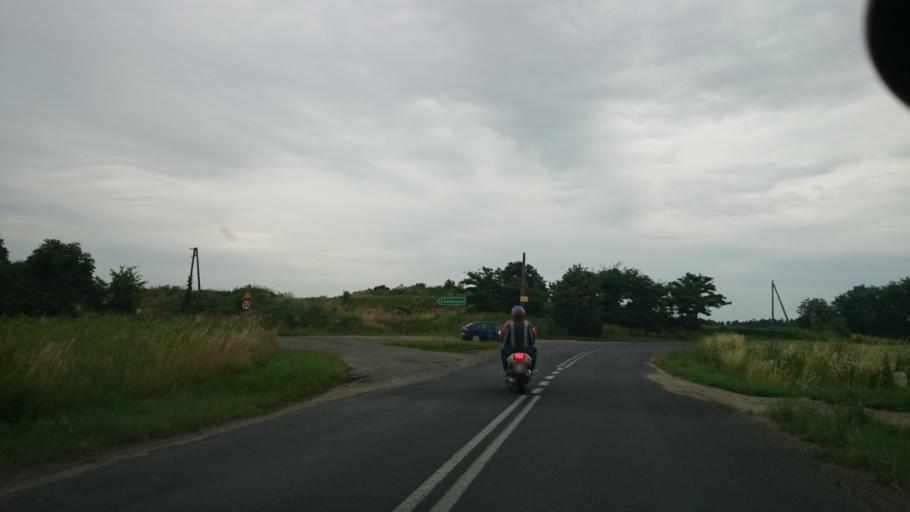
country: PL
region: Lower Silesian Voivodeship
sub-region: Powiat strzelinski
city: Przeworno
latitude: 50.6651
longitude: 17.2665
